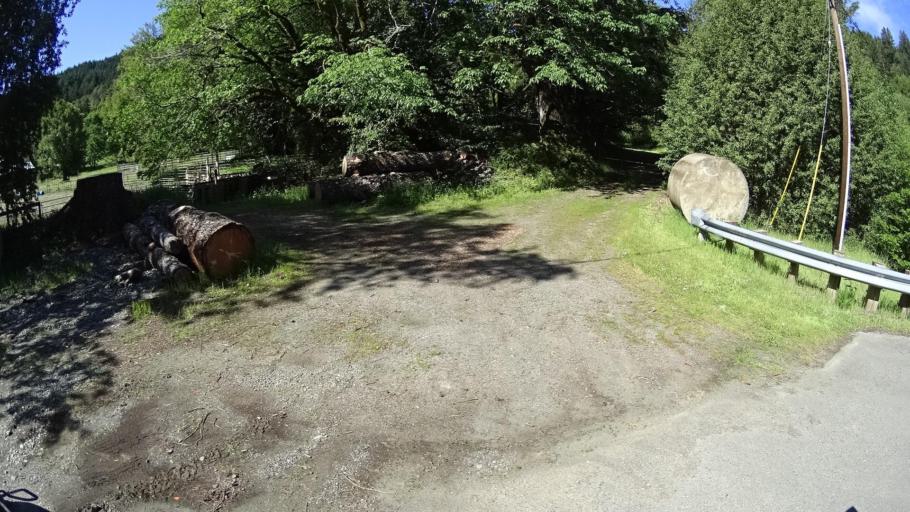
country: US
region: California
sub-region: Humboldt County
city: Rio Dell
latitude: 40.2849
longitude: -124.2514
